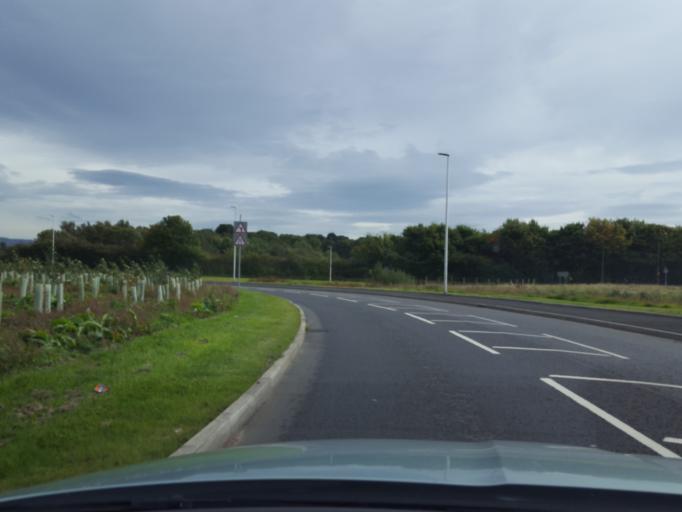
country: GB
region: Scotland
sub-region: West Lothian
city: Mid Calder
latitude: 55.9107
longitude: -3.4897
